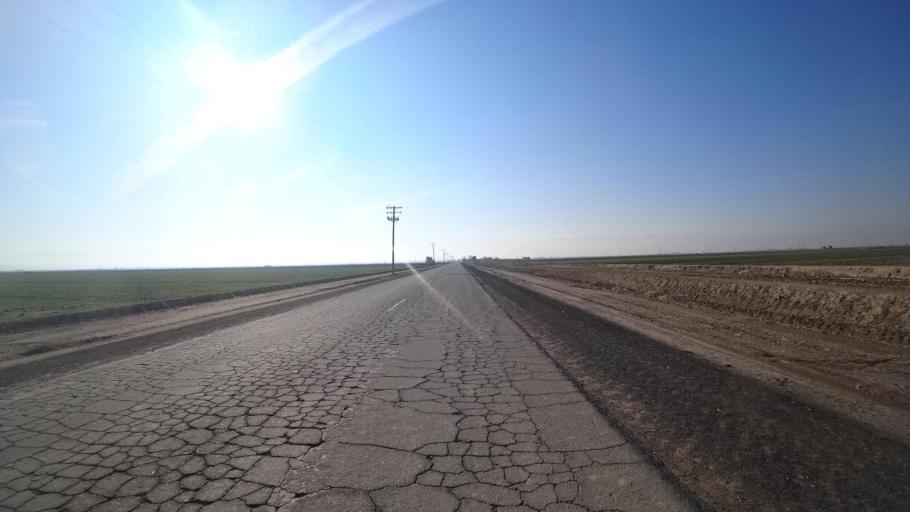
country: US
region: California
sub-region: Kern County
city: Weedpatch
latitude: 35.1856
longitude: -118.9677
